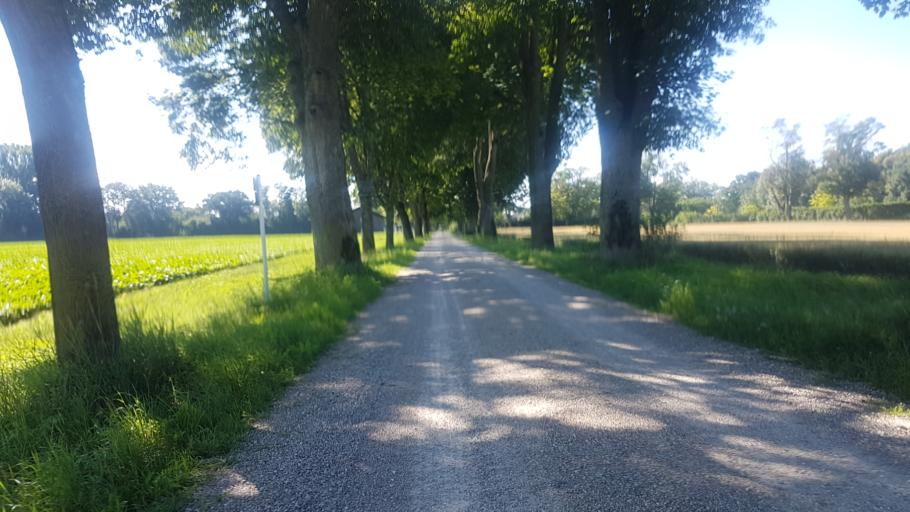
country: DE
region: Bavaria
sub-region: Upper Bavaria
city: Bergheim
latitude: 48.7294
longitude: 11.2708
